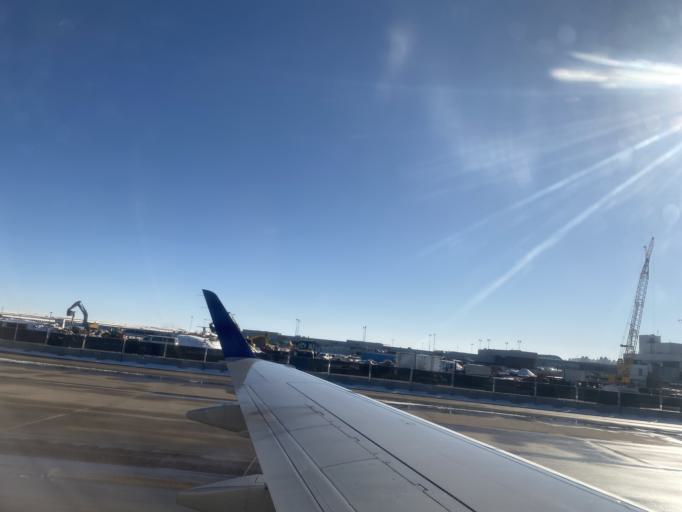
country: US
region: Colorado
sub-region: Weld County
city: Lochbuie
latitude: 39.8606
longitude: -104.6662
